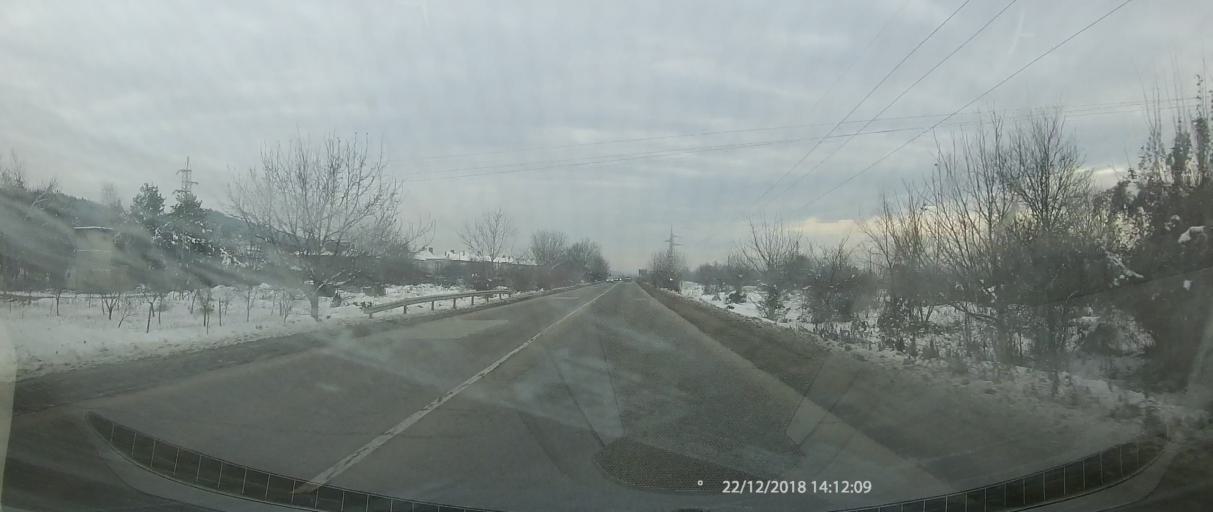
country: BG
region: Pleven
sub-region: Obshtina Pleven
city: Pleven
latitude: 43.4446
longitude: 24.5778
